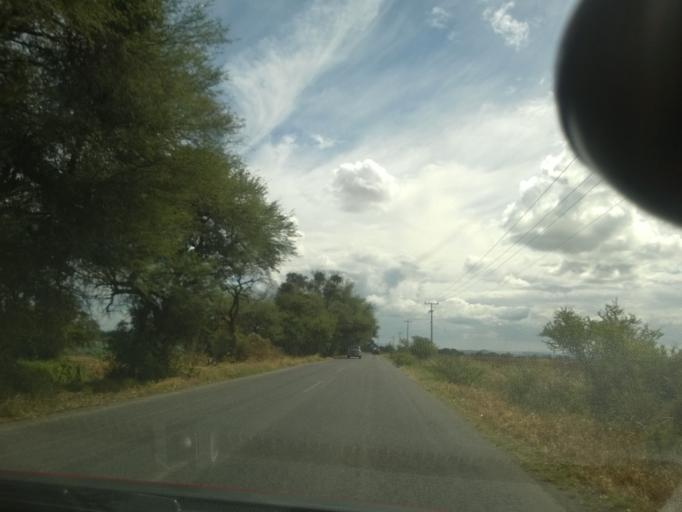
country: MX
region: Guanajuato
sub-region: Leon
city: El CERESO
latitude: 20.9815
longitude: -101.6532
